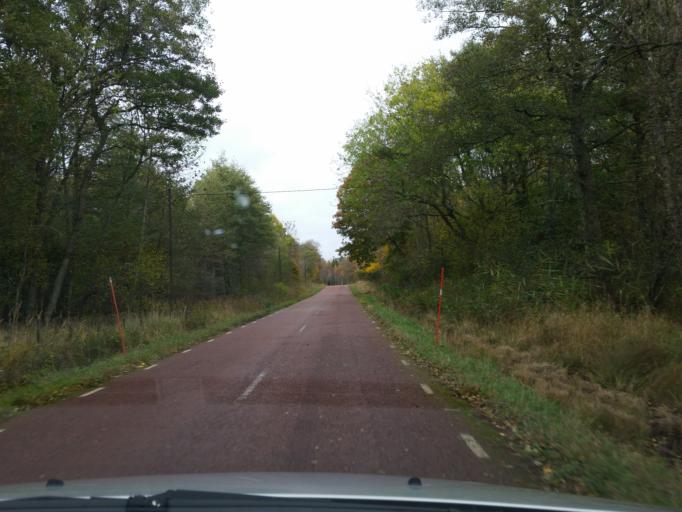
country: AX
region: Alands landsbygd
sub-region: Lemland
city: Lemland
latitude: 59.9762
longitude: 20.1829
